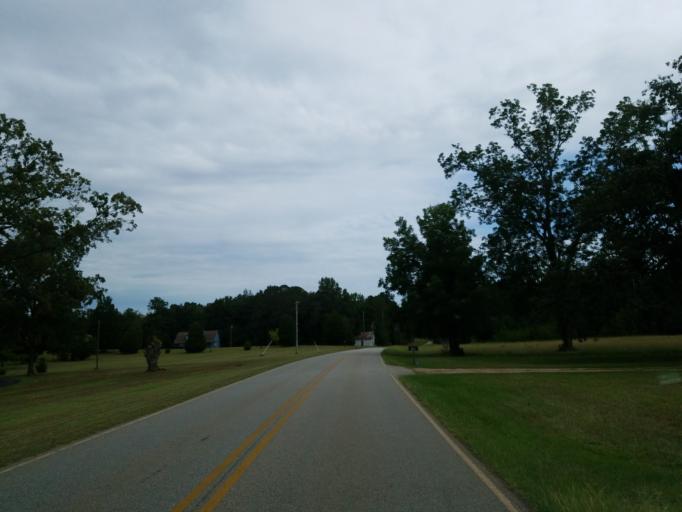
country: US
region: Georgia
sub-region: Monroe County
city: Forsyth
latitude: 32.9185
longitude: -83.9158
